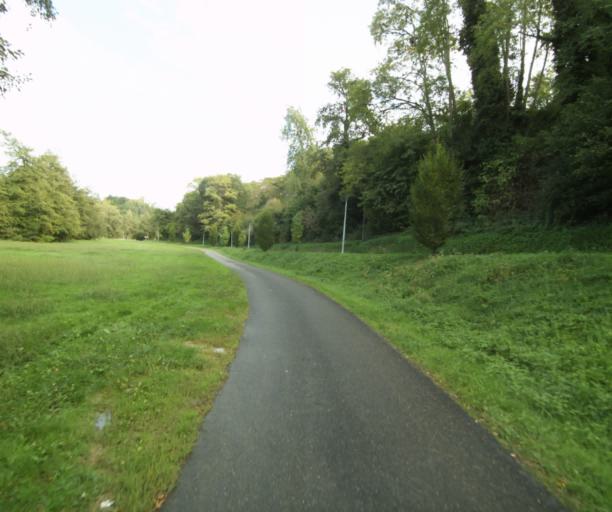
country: FR
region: Midi-Pyrenees
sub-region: Departement du Gers
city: Eauze
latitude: 43.8697
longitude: 0.1078
